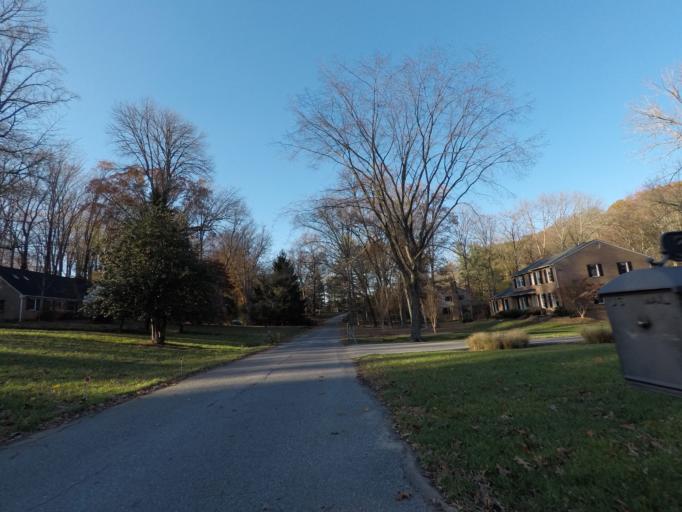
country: US
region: Maryland
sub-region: Howard County
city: Ellicott City
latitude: 39.2846
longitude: -76.7930
